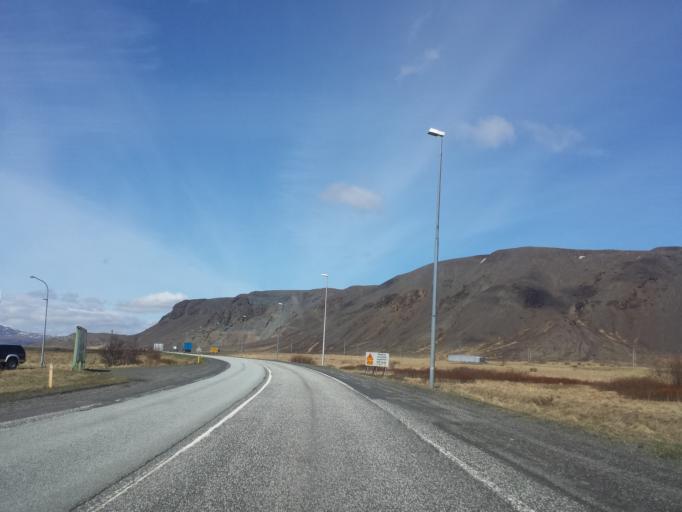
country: IS
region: South
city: Selfoss
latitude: 63.9486
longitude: -21.0148
